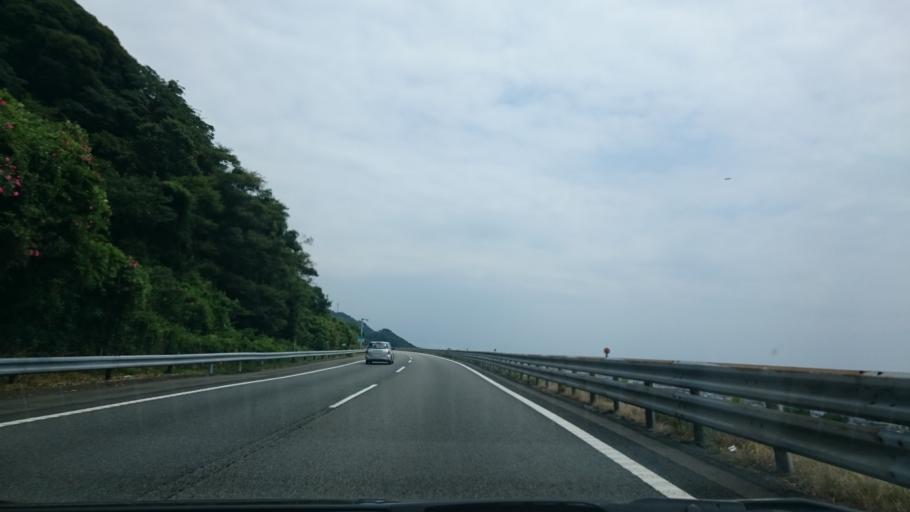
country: JP
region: Shizuoka
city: Fujinomiya
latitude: 35.1170
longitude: 138.5876
